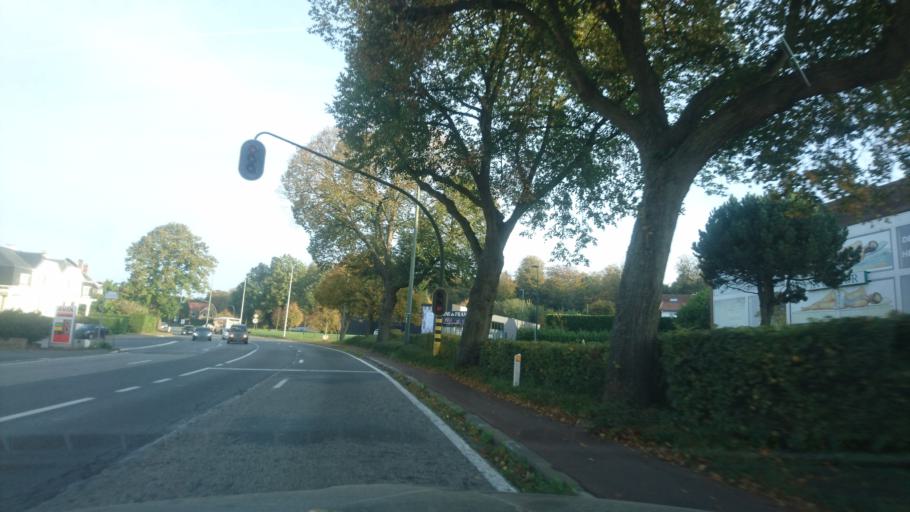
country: BE
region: Wallonia
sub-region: Province du Brabant Wallon
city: Waterloo
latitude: 50.7471
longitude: 4.3947
